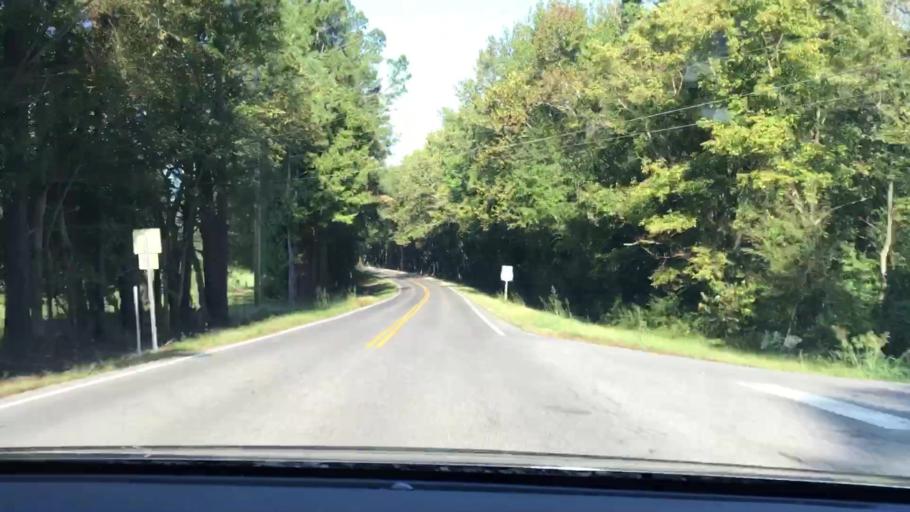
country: US
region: Kentucky
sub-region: Marshall County
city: Benton
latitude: 36.7675
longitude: -88.2740
